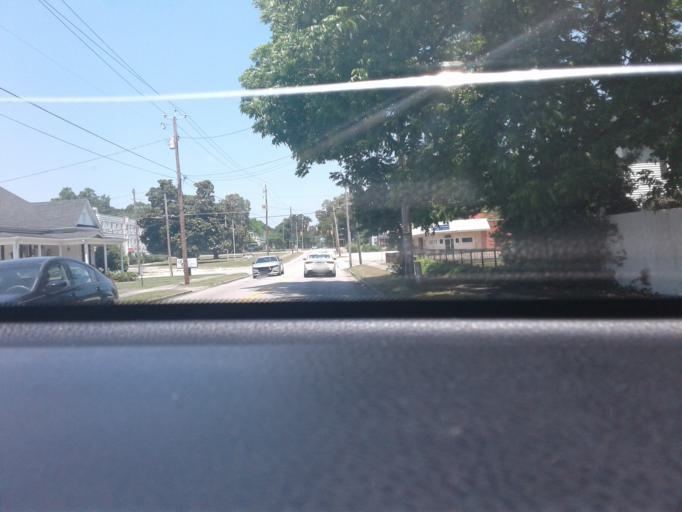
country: US
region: North Carolina
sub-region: Harnett County
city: Dunn
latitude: 35.3114
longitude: -78.6152
